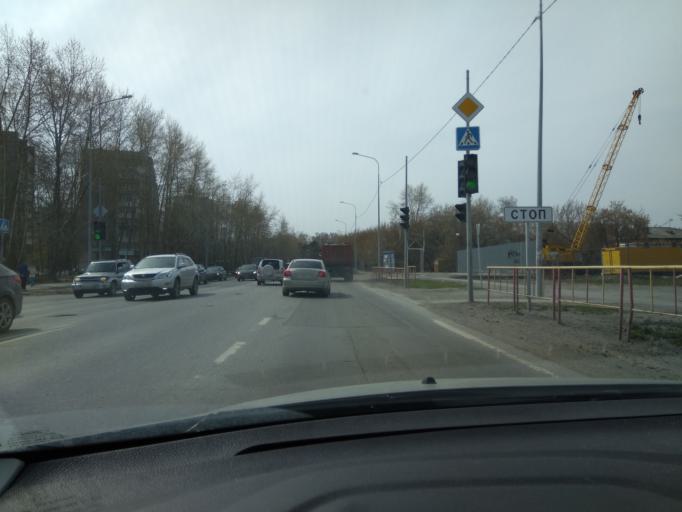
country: RU
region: Tjumen
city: Melioratorov
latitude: 57.1831
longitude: 65.5803
